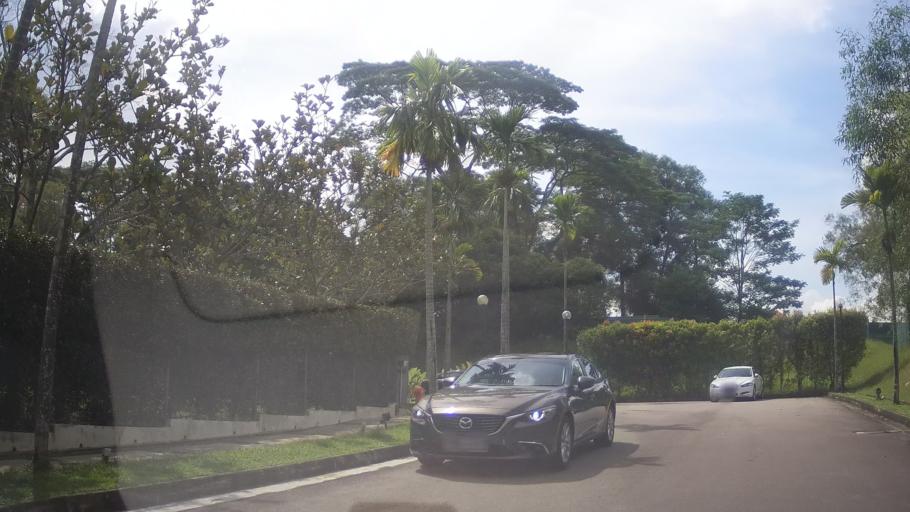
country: MY
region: Johor
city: Johor Bahru
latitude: 1.4162
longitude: 103.7560
